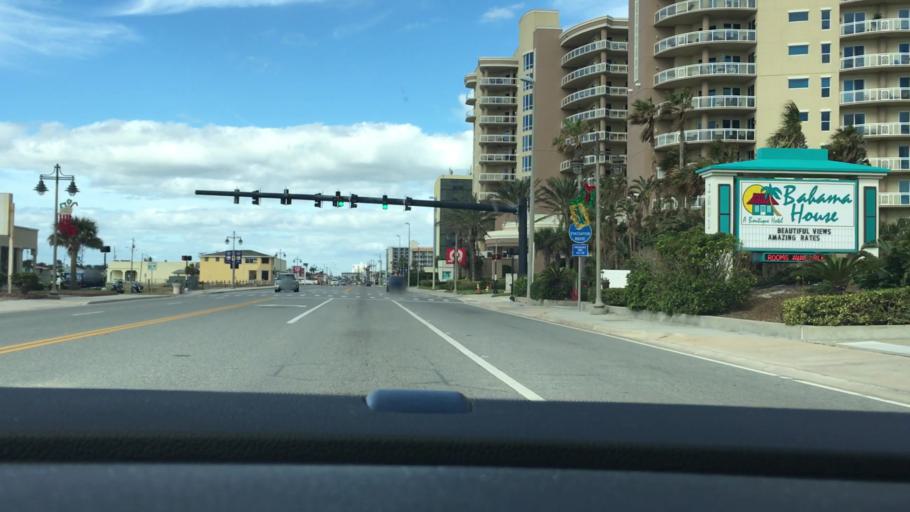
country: US
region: Florida
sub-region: Volusia County
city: Daytona Beach
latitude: 29.2026
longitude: -80.9963
